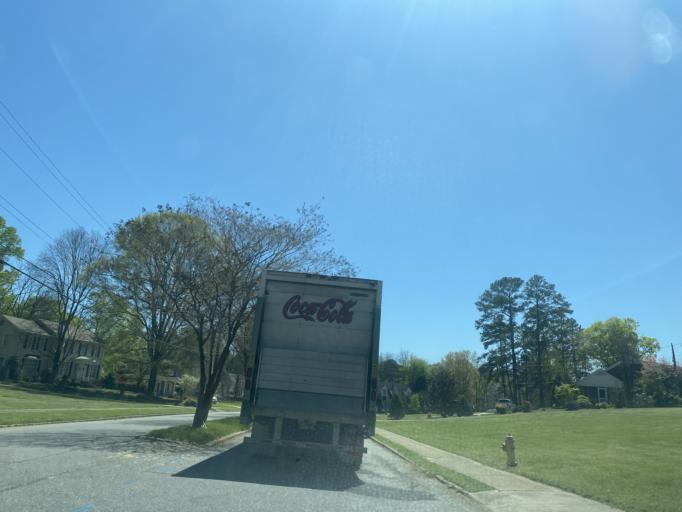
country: US
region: South Carolina
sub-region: Cherokee County
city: Gaffney
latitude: 35.0613
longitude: -81.6462
